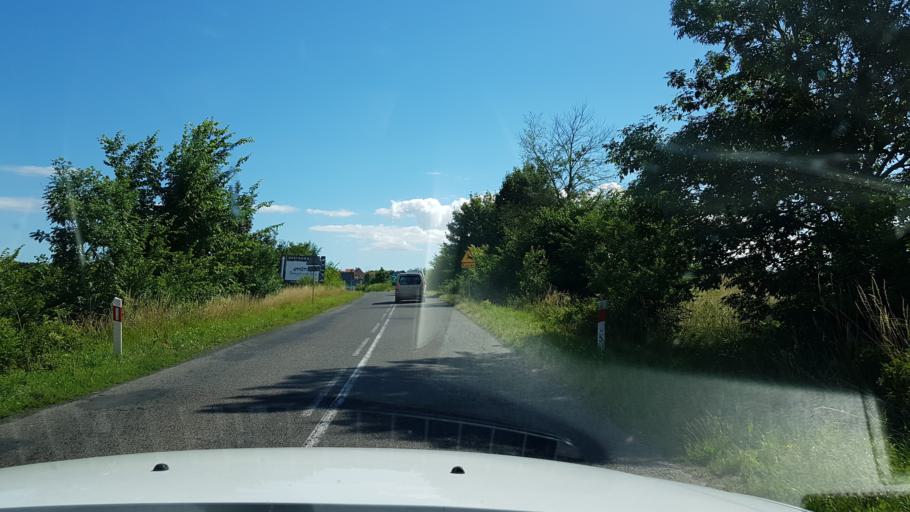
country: PL
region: West Pomeranian Voivodeship
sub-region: Powiat gryficki
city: Trzebiatow
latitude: 54.0505
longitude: 15.2480
